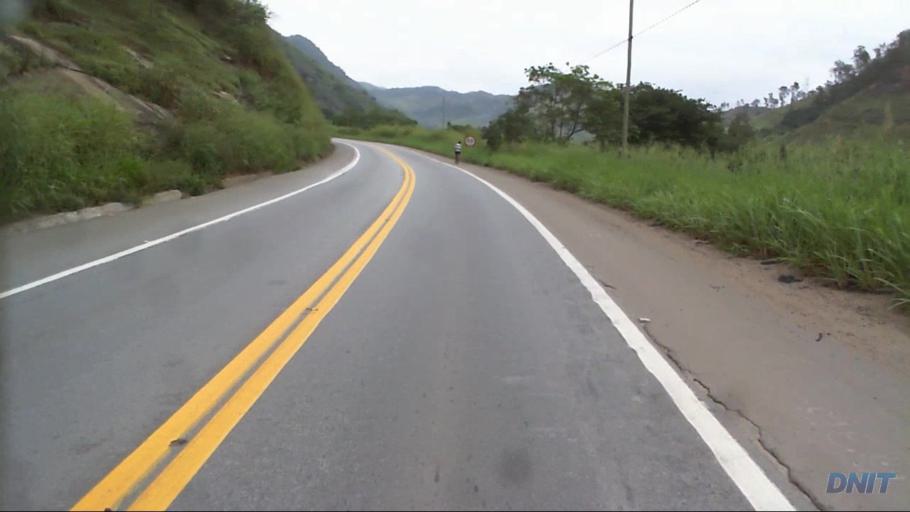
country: BR
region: Minas Gerais
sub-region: Timoteo
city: Timoteo
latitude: -19.5553
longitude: -42.7105
